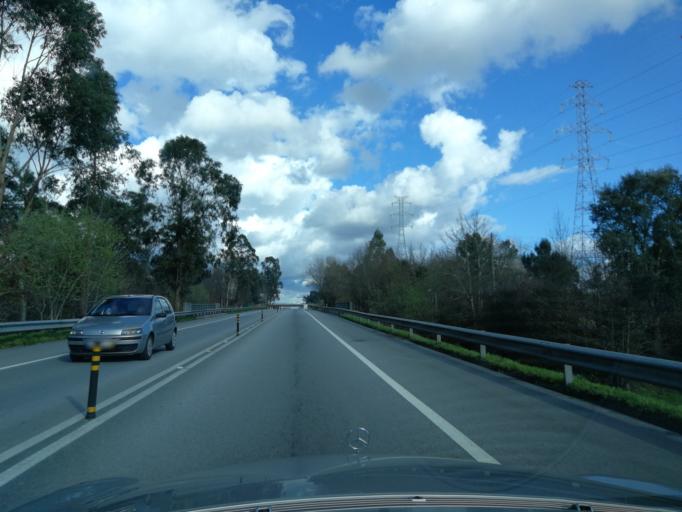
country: PT
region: Braga
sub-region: Vila Verde
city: Vila Verde
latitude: 41.6170
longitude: -8.4441
